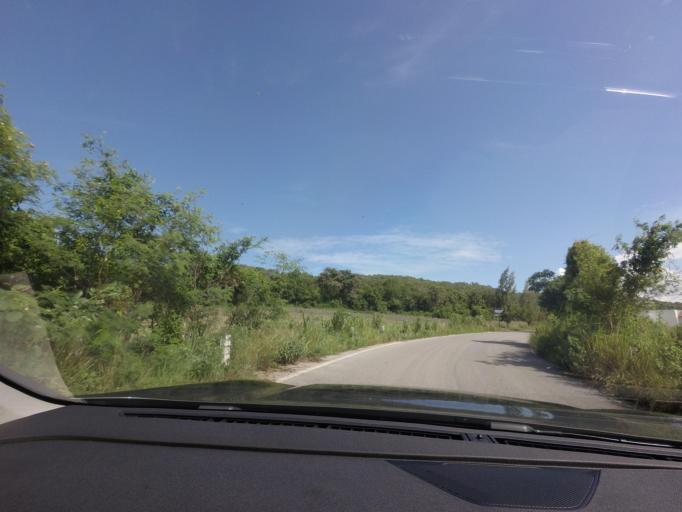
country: TH
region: Prachuap Khiri Khan
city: Hua Hin
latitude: 12.4878
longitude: 99.9424
